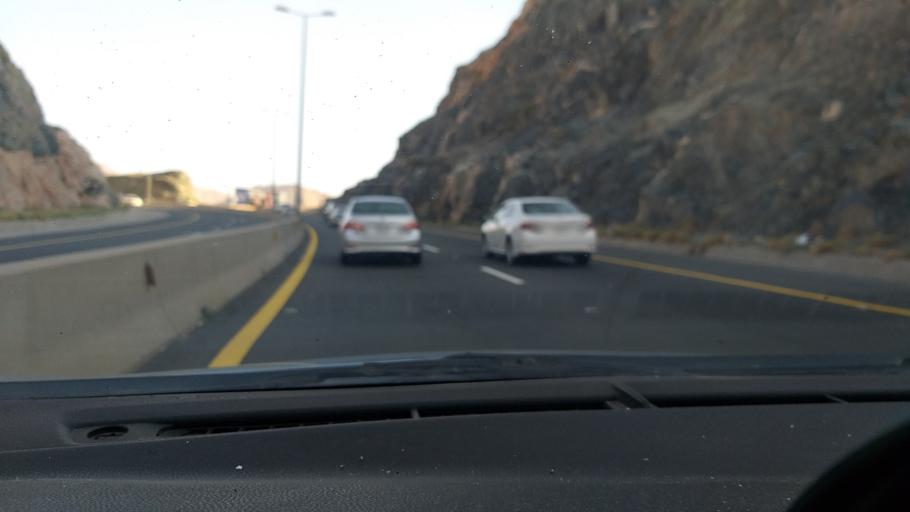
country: SA
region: Makkah
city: Al Hada
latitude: 21.3530
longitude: 40.2404
